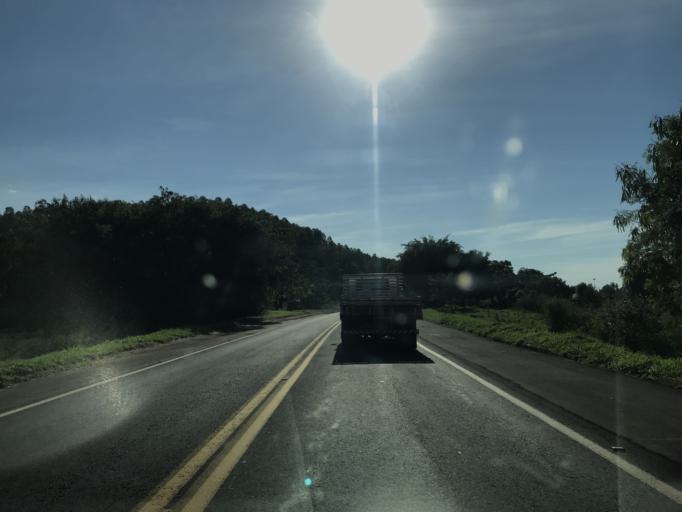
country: BR
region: Parana
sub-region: Ipora
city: Ipora
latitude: -23.9238
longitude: -53.5714
